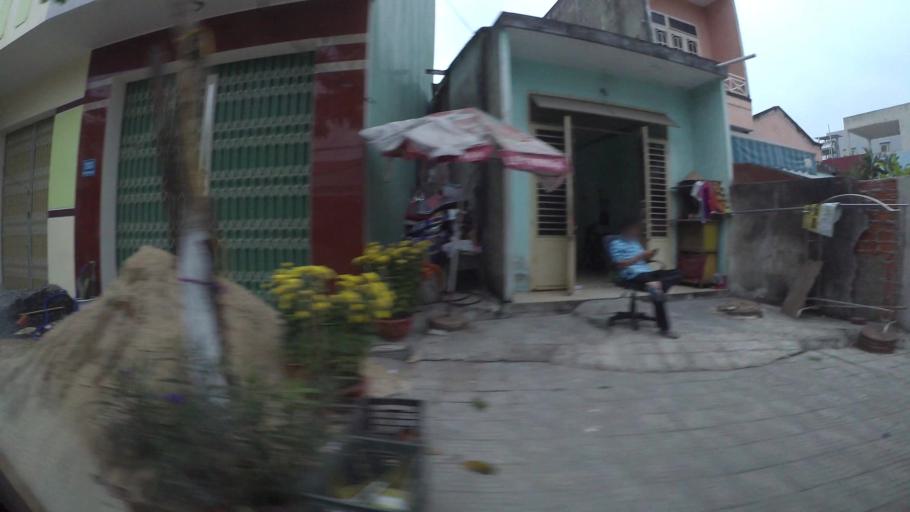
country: VN
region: Da Nang
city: Thanh Khe
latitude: 16.0488
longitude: 108.1764
